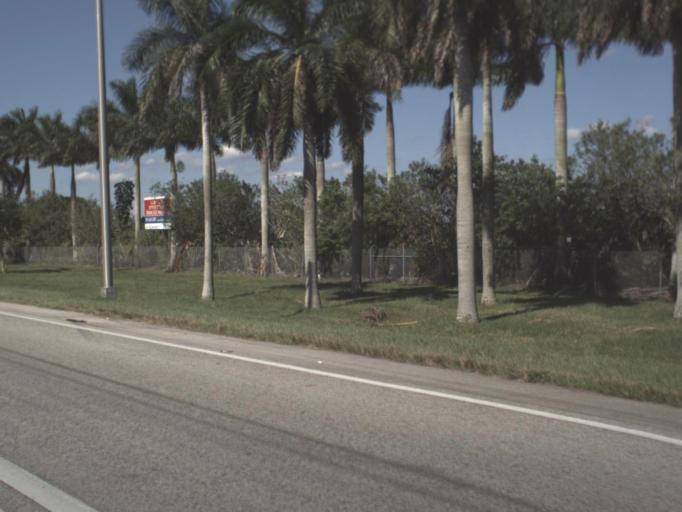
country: US
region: Florida
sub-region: Miami-Dade County
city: Goulds
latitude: 25.5315
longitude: -80.3777
